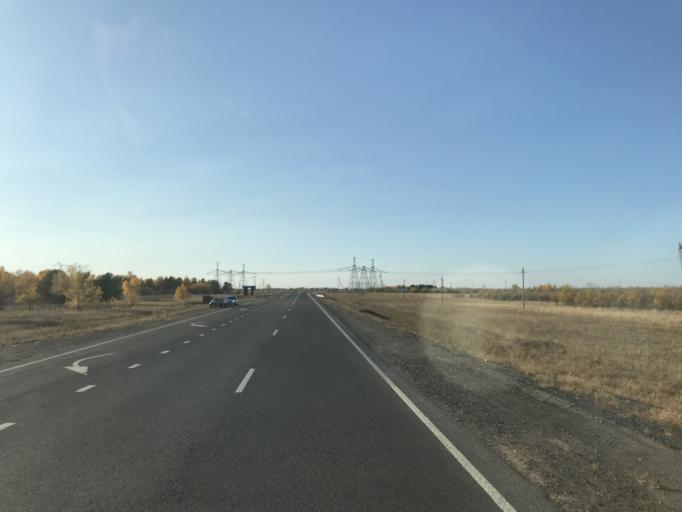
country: KZ
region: Pavlodar
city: Koktobe
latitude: 51.9070
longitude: 77.3658
